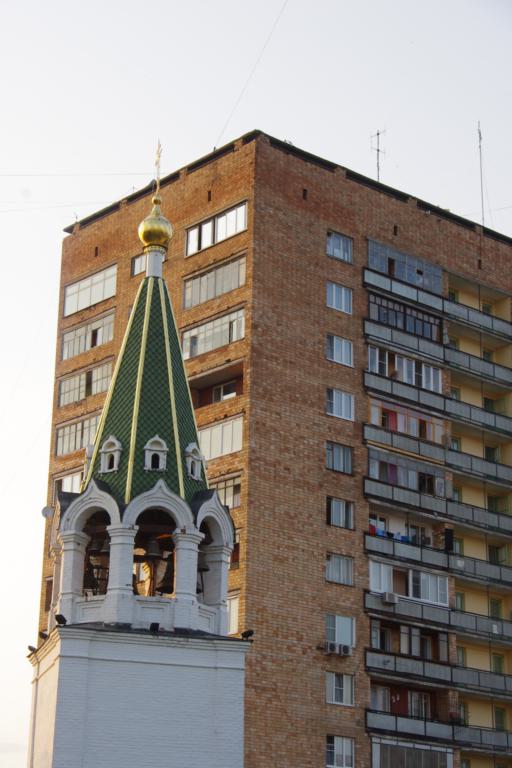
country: RU
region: Nizjnij Novgorod
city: Nizhniy Novgorod
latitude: 56.3260
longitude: 43.9902
